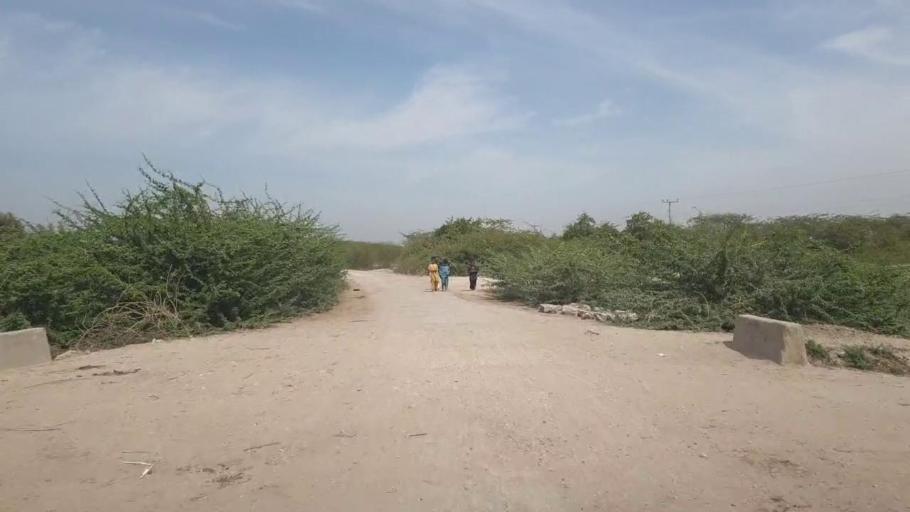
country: PK
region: Sindh
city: Kunri
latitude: 25.2351
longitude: 69.6696
